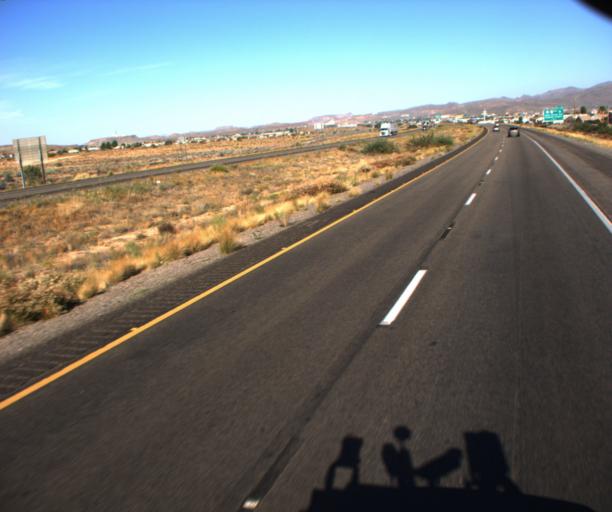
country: US
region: Arizona
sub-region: Mohave County
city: New Kingman-Butler
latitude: 35.2171
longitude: -113.9941
